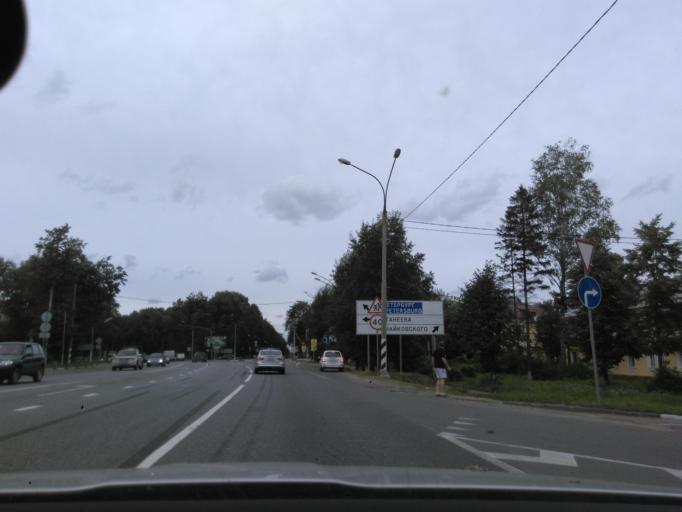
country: RU
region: Moskovskaya
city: Klin
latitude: 56.3260
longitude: 36.7537
